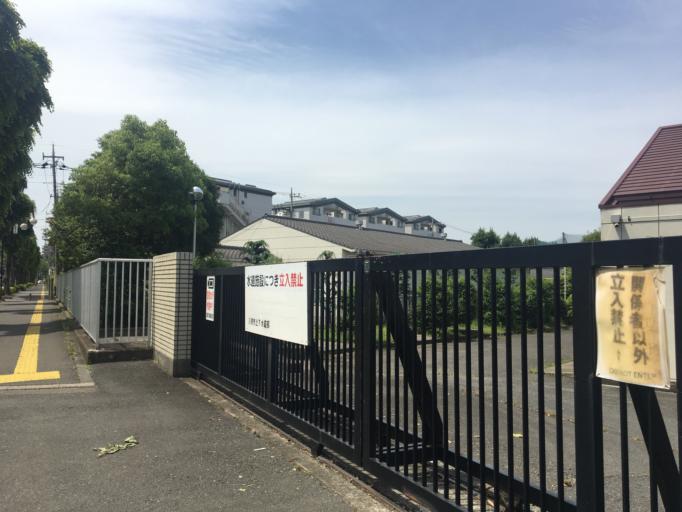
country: JP
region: Saitama
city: Sayama
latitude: 35.8361
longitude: 139.3948
